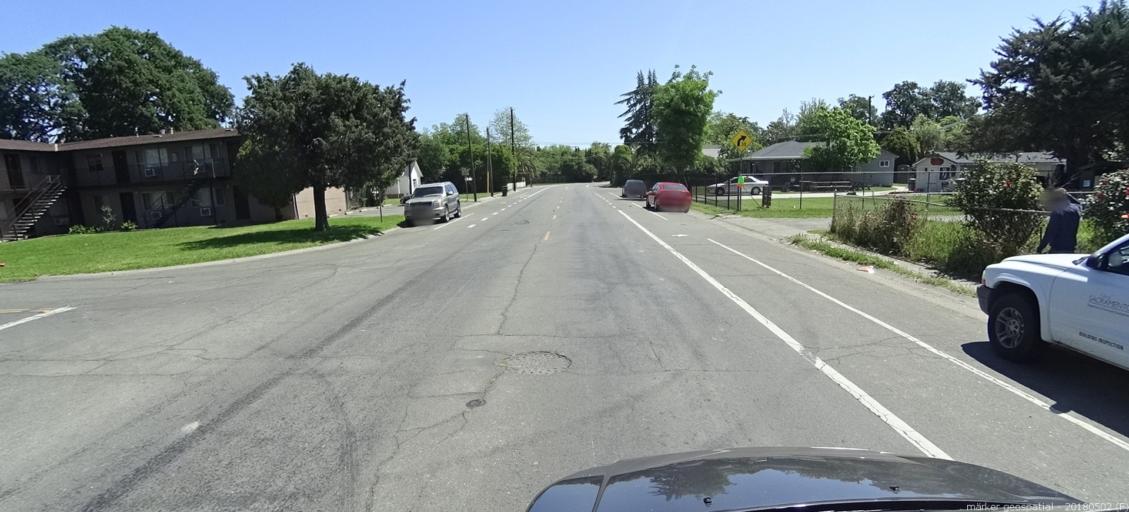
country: US
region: California
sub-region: Sacramento County
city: Arden-Arcade
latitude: 38.6265
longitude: -121.4378
